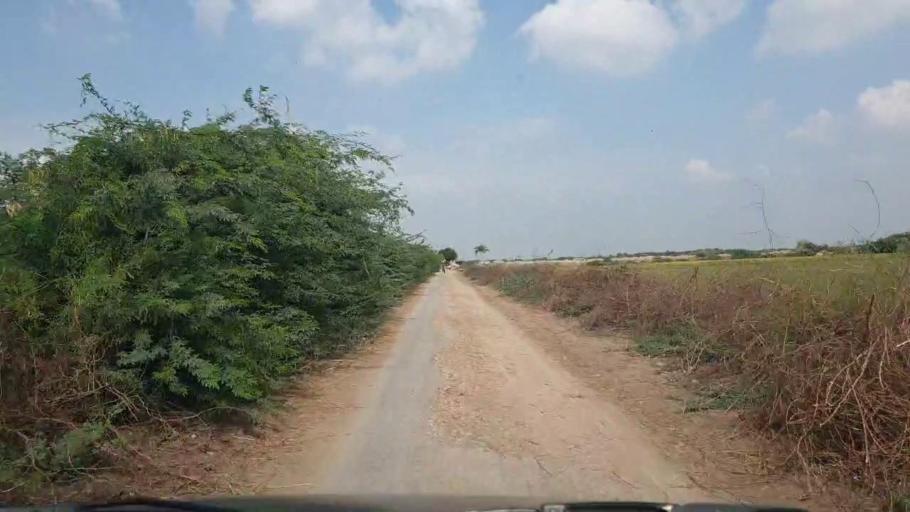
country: PK
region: Sindh
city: Badin
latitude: 24.4698
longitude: 68.5902
